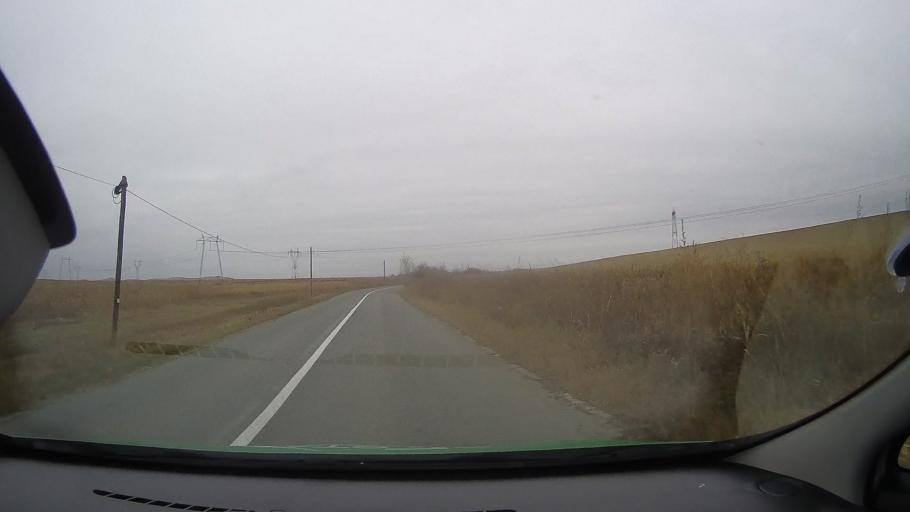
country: RO
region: Constanta
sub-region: Comuna Silistea
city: Silistea
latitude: 44.4339
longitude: 28.2198
